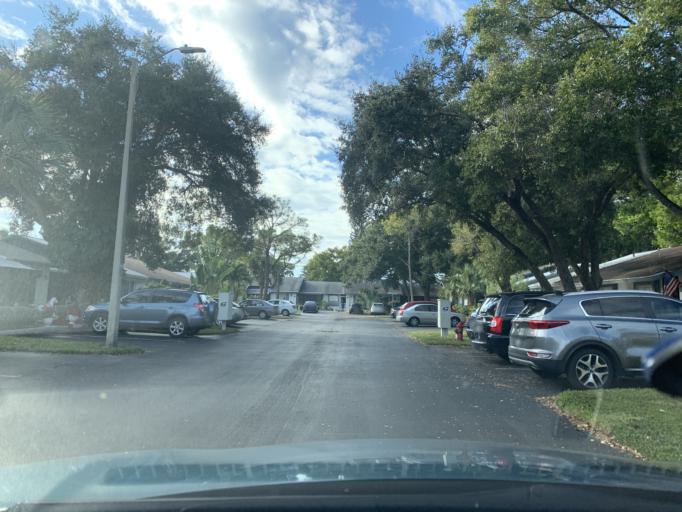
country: US
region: Florida
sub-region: Pinellas County
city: Kenneth City
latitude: 27.8221
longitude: -82.7398
